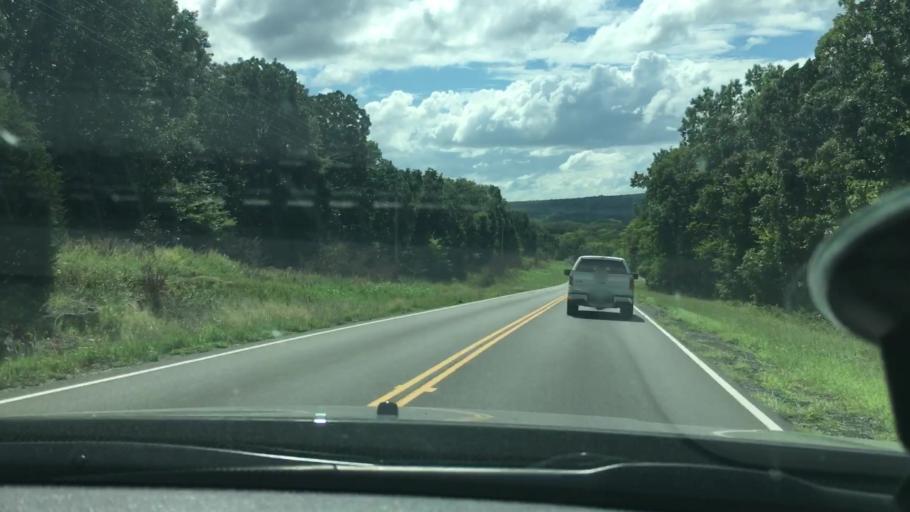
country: US
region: Oklahoma
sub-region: Sequoyah County
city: Vian
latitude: 35.6487
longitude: -94.9553
